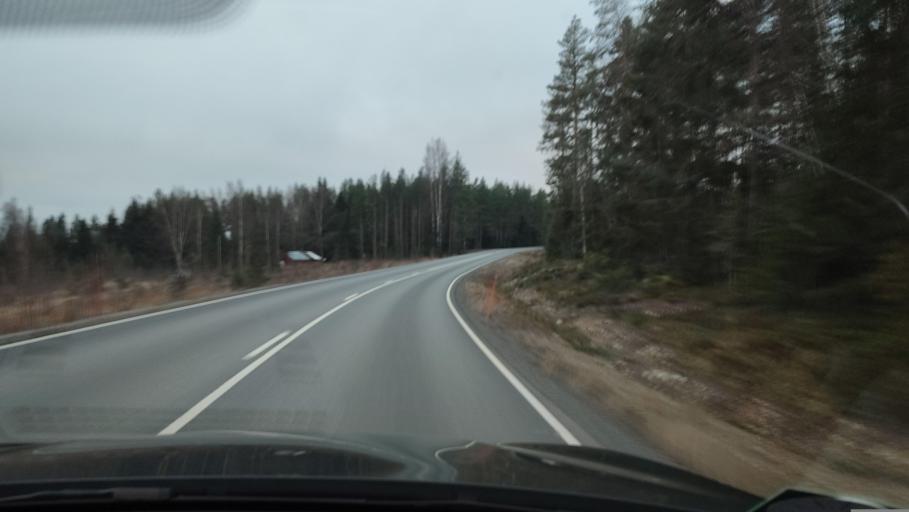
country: FI
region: Southern Ostrobothnia
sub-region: Suupohja
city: Karijoki
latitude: 62.2977
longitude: 21.6828
